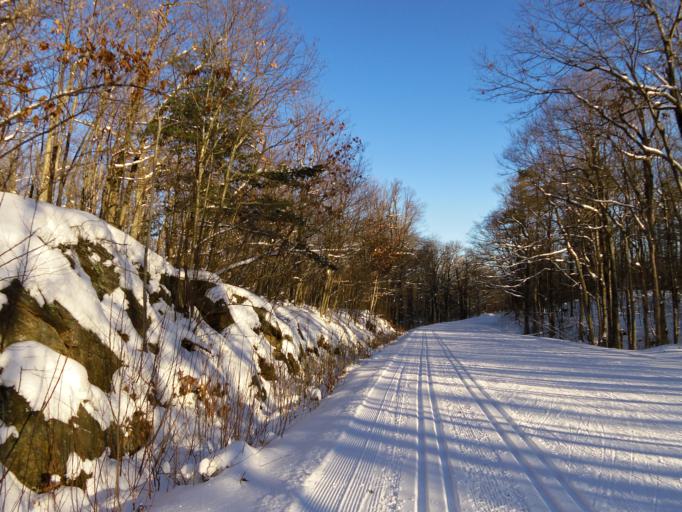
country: CA
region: Quebec
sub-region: Outaouais
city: Wakefield
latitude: 45.5049
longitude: -75.8980
